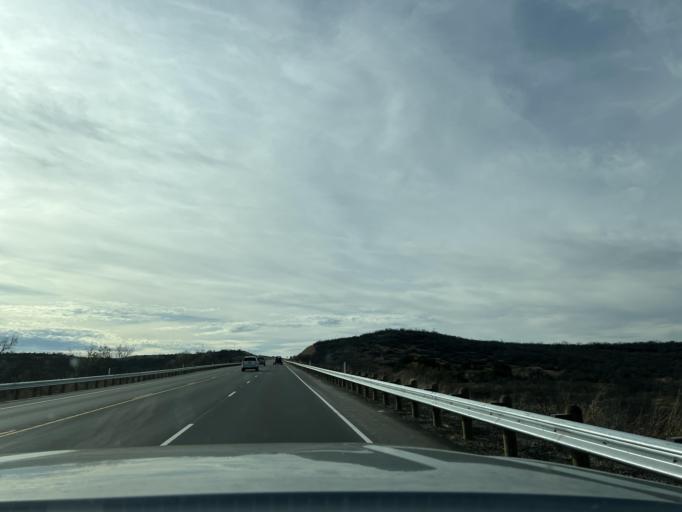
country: US
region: Texas
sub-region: Shackelford County
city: Albany
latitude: 32.7099
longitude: -99.3682
